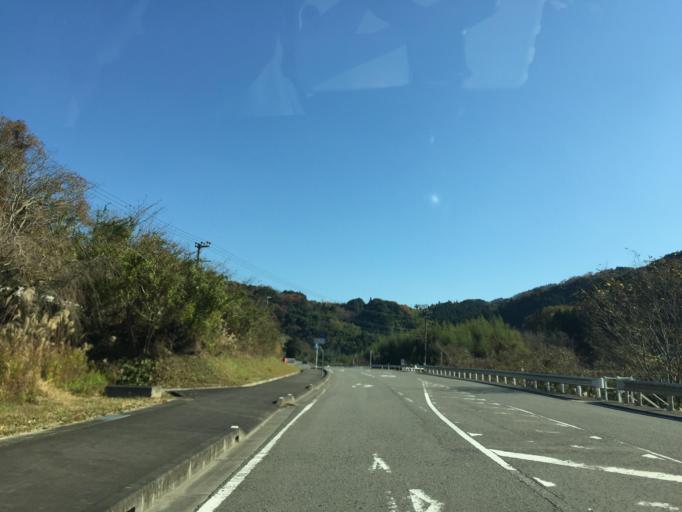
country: JP
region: Wakayama
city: Iwade
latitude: 34.1442
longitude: 135.3527
